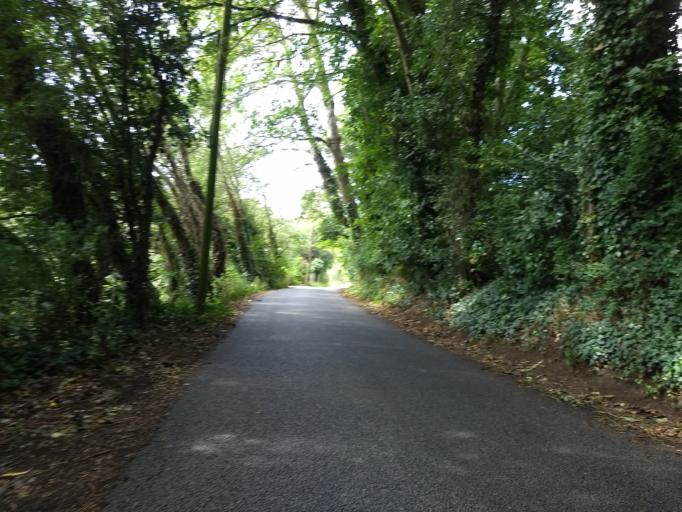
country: GB
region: England
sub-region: Isle of Wight
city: Newport
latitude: 50.6839
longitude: -1.2954
